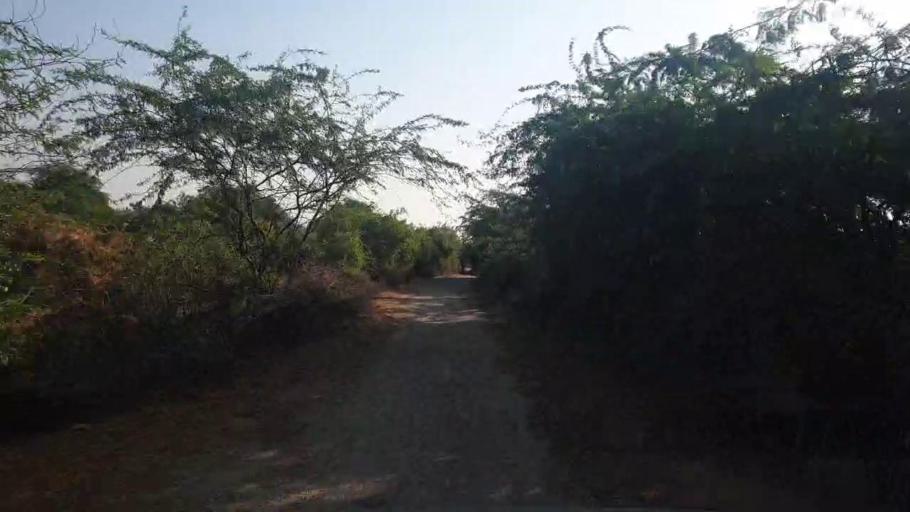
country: PK
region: Sindh
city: Tando Bago
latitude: 24.7452
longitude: 68.9291
